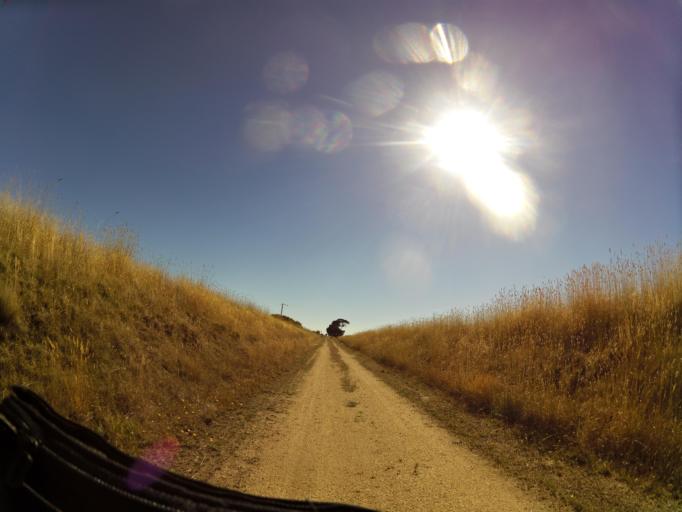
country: AU
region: Victoria
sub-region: Ballarat North
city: Delacombe
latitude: -37.6924
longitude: 143.3746
